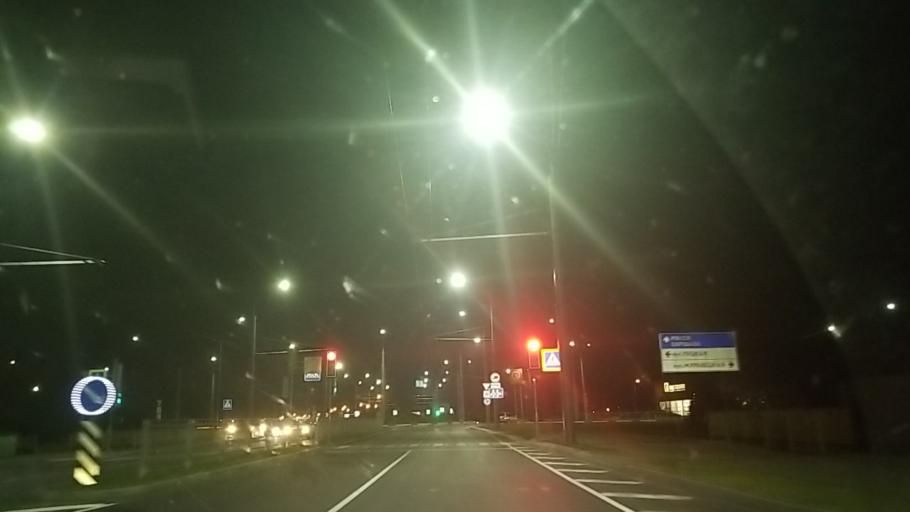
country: BY
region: Brest
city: Brest
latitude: 52.0763
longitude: 23.7677
